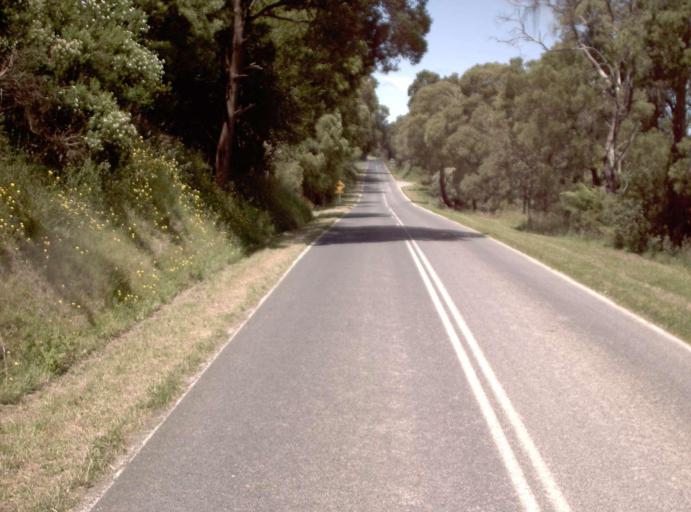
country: AU
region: Victoria
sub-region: Bass Coast
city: North Wonthaggi
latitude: -38.7237
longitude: 146.1210
